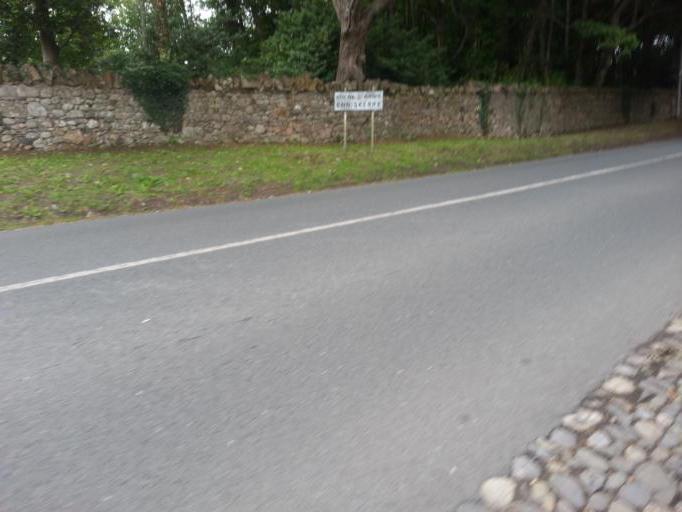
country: IE
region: Leinster
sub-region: Wicklow
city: Enniskerry
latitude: 53.1886
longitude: -6.1697
